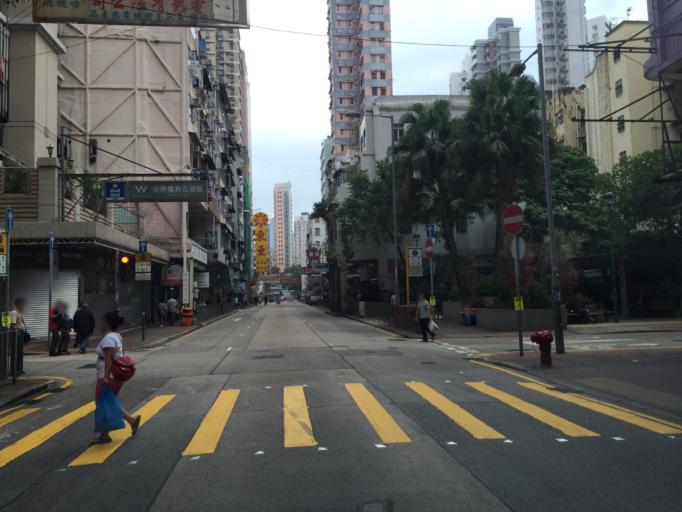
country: HK
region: Kowloon City
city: Kowloon
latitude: 22.3118
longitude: 114.1698
